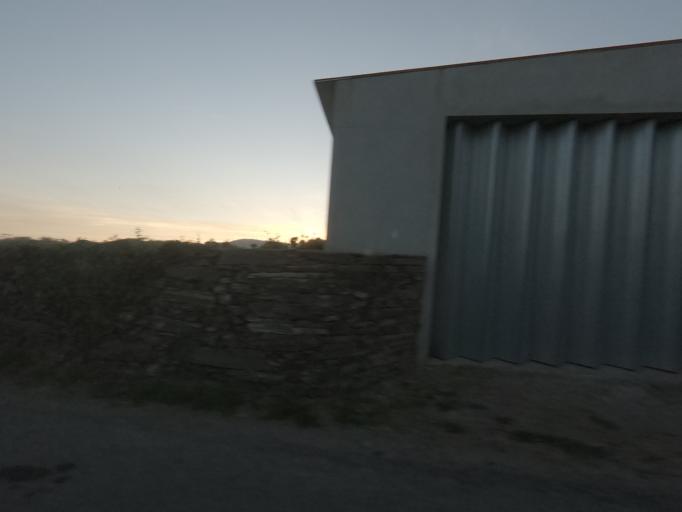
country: PT
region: Vila Real
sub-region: Peso da Regua
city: Peso da Regua
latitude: 41.1732
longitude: -7.7316
